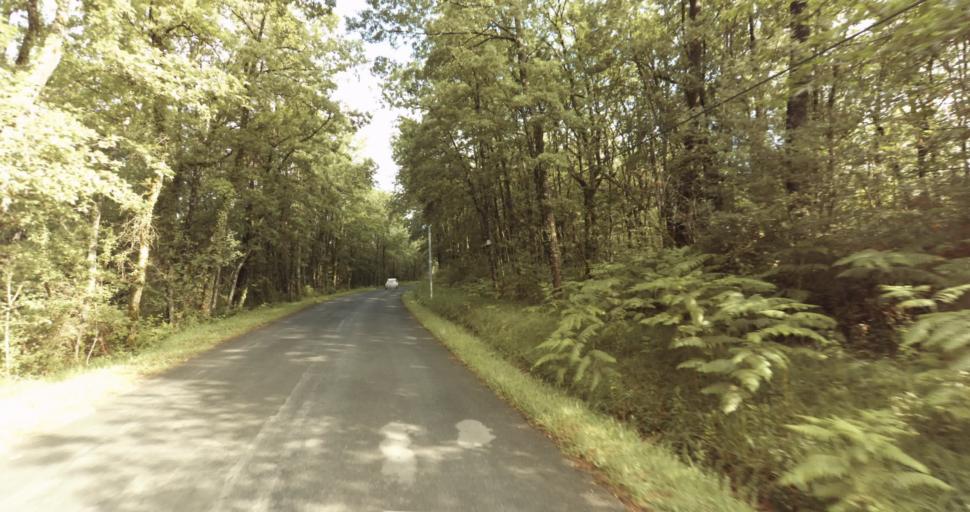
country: FR
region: Aquitaine
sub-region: Departement de la Dordogne
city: Le Bugue
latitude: 44.9275
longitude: 0.8207
